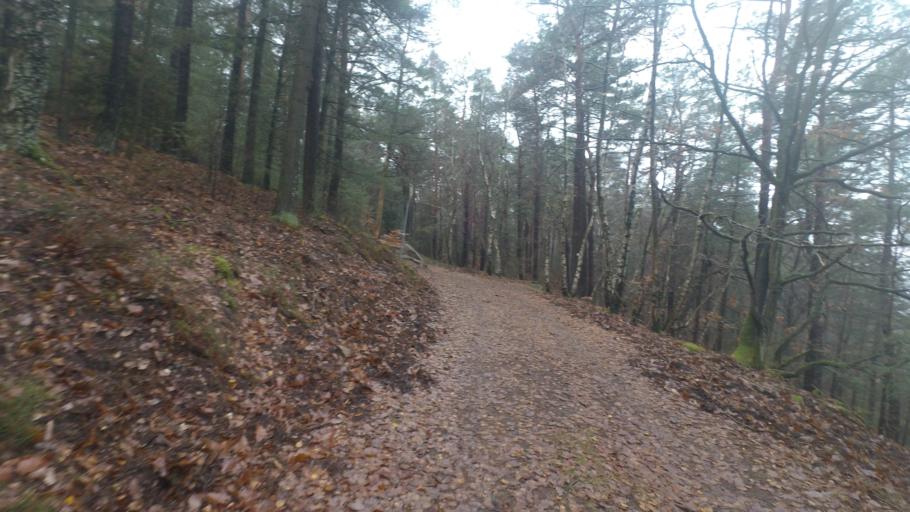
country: DE
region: Rheinland-Pfalz
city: Lindenberg
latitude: 49.3979
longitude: 8.1322
